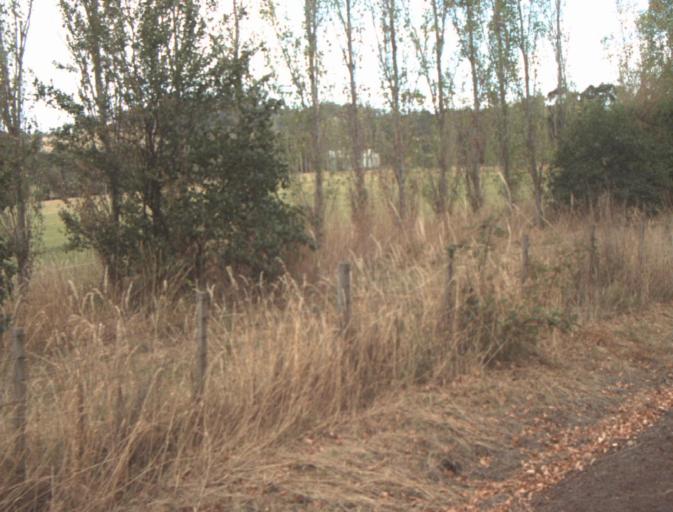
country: AU
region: Tasmania
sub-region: Launceston
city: Mayfield
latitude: -41.2916
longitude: 146.9909
